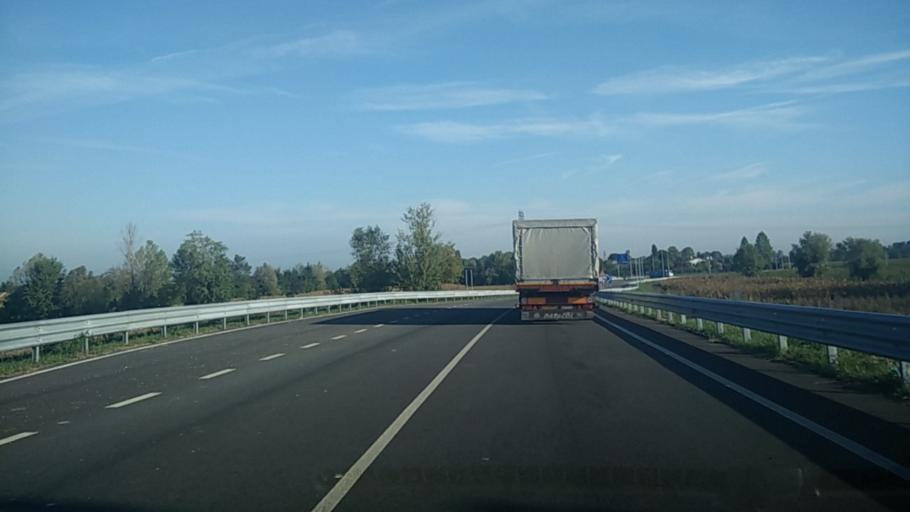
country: IT
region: Veneto
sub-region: Provincia di Venezia
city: Peseggia-Gardigiano
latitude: 45.5466
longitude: 12.1792
